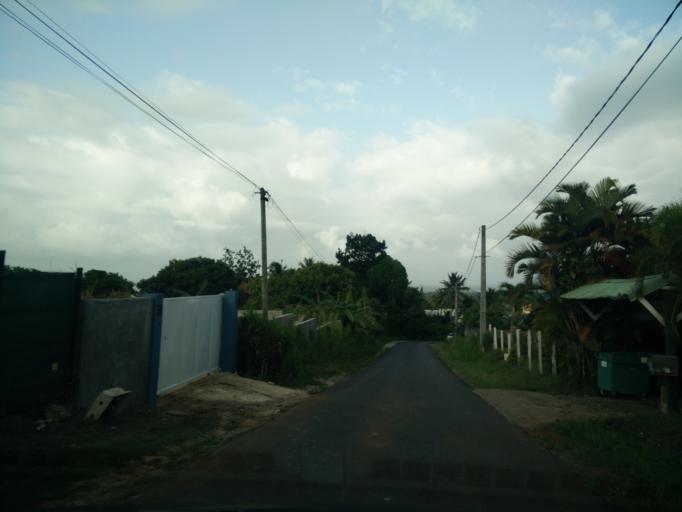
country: GP
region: Guadeloupe
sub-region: Guadeloupe
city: Petit-Bourg
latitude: 16.1848
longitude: -61.6130
